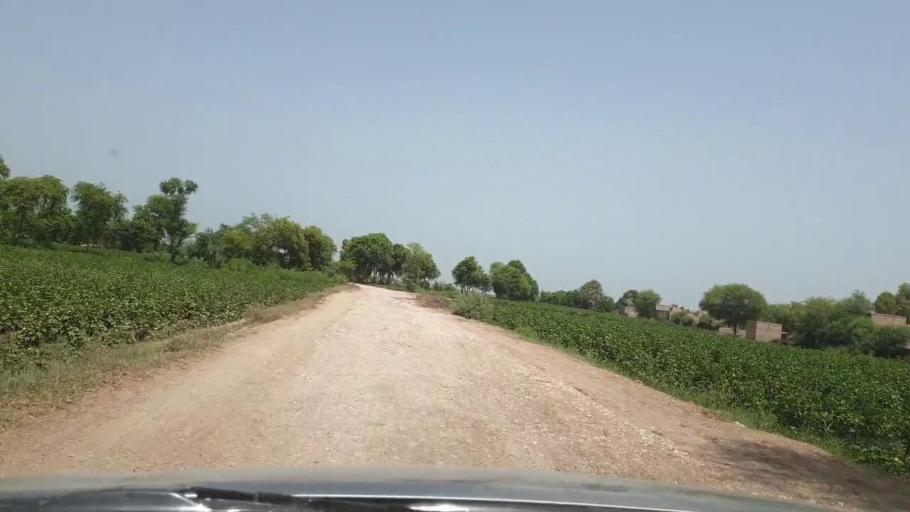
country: PK
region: Sindh
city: Pano Aqil
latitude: 27.8072
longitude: 69.2316
